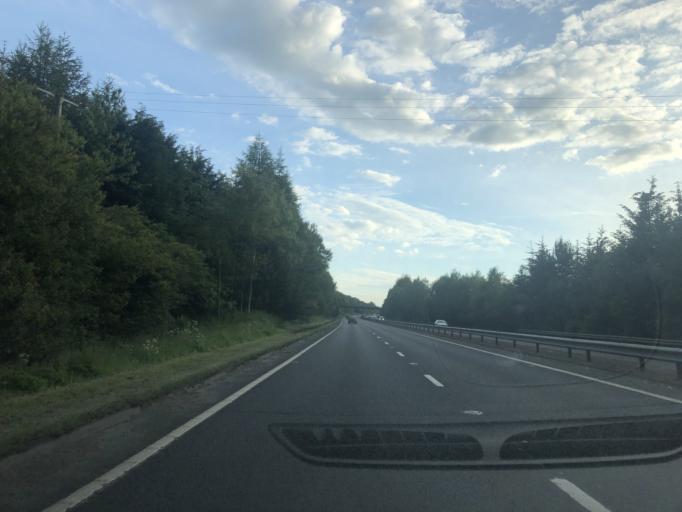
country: GB
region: Scotland
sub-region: Fife
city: Cardenden
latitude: 56.1303
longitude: -3.2505
